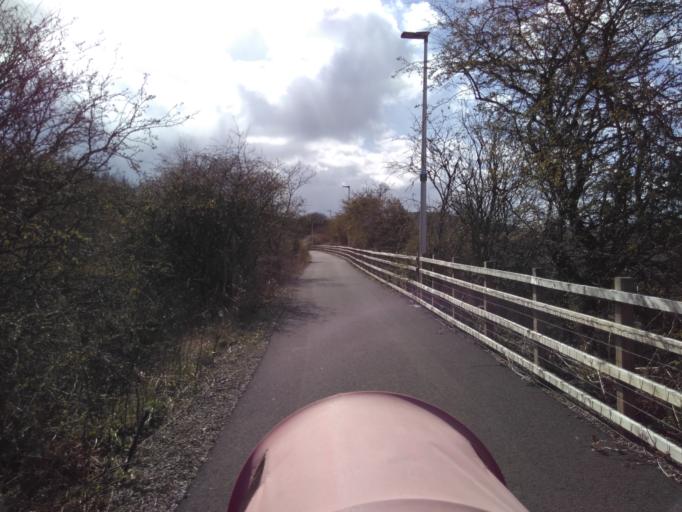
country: GB
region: Scotland
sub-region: Midlothian
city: Loanhead
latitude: 55.8910
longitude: -3.1427
